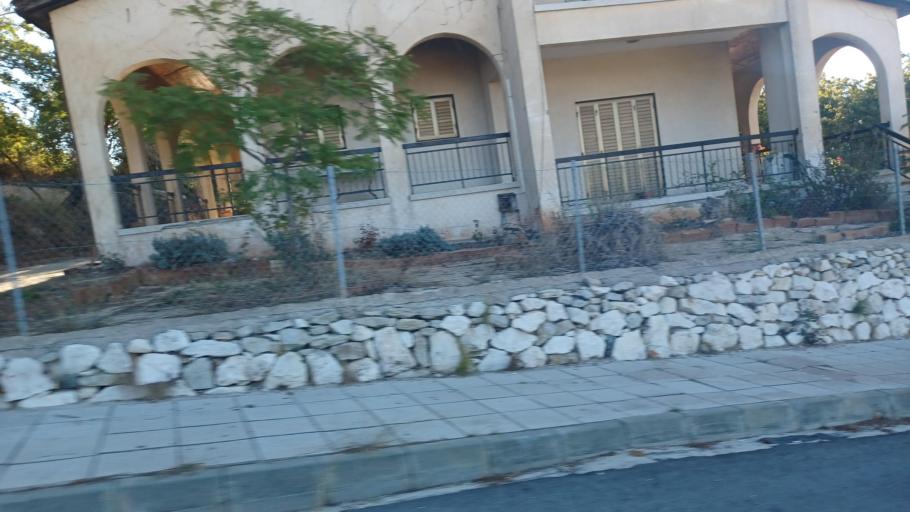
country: CY
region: Pafos
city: Mesogi
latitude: 34.7977
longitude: 32.4870
